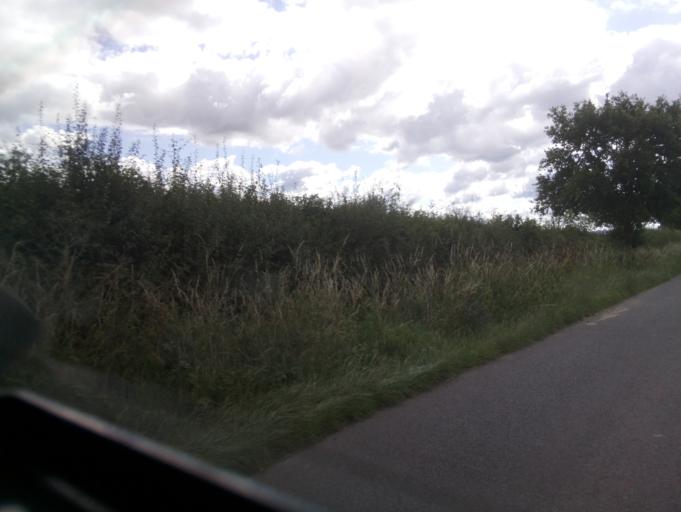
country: GB
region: England
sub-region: Gloucestershire
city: Mitcheldean
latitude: 51.8445
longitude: -2.4144
